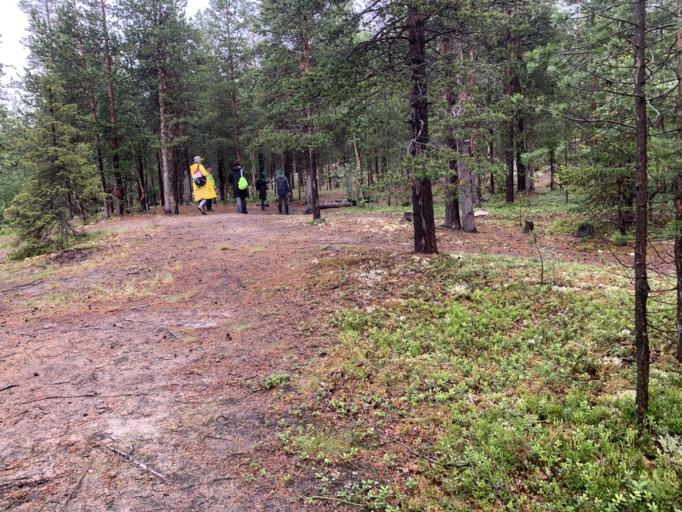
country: RU
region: Murmansk
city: Monchegorsk
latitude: 67.9490
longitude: 33.0237
